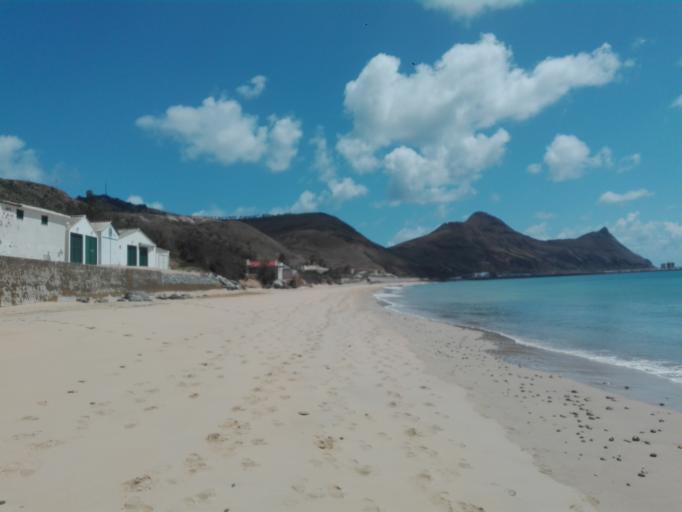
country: PT
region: Madeira
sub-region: Porto Santo
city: Vila de Porto Santo
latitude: 33.0606
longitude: -16.3287
